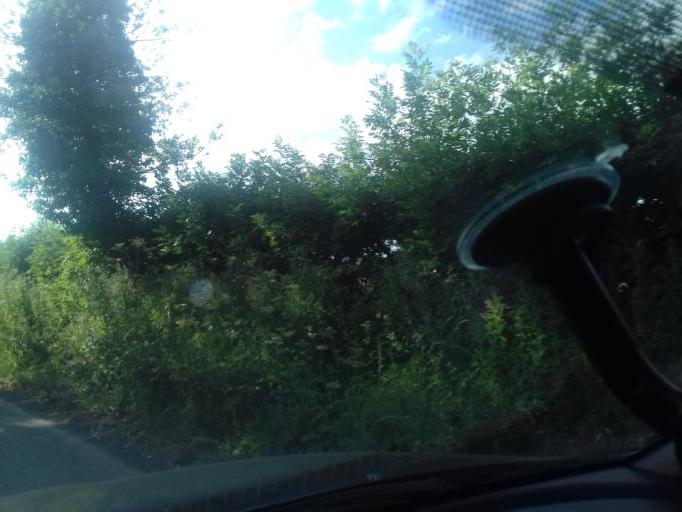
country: IE
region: Leinster
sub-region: An Mhi
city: Dunboyne
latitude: 53.4382
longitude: -6.4414
